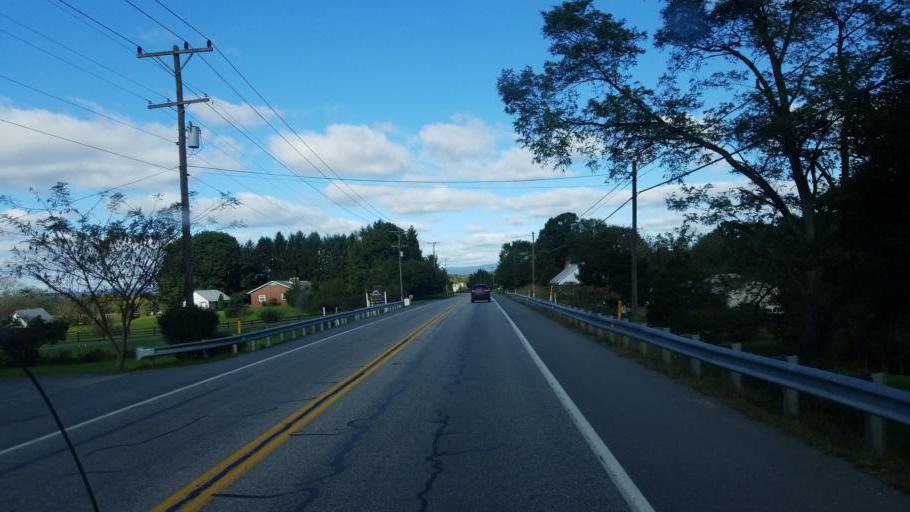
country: US
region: Pennsylvania
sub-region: Franklin County
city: Greencastle
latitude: 39.7951
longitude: -77.7646
